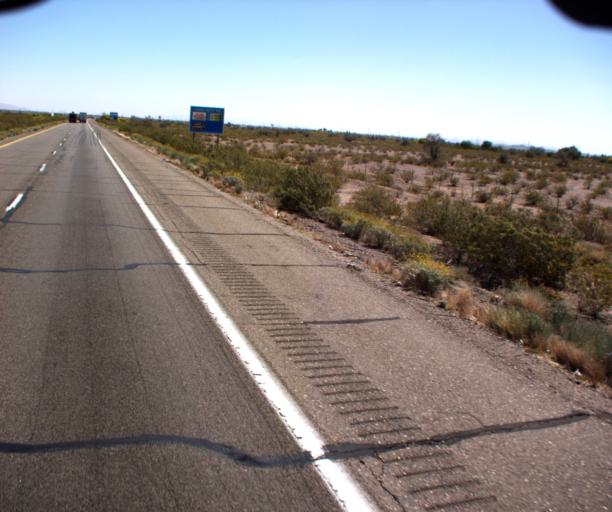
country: US
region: Arizona
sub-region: Maricopa County
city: Buckeye
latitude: 33.5007
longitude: -112.9542
